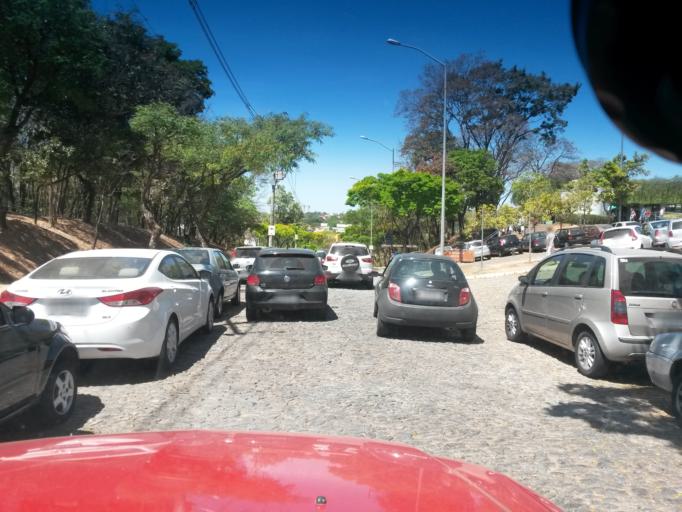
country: BR
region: Minas Gerais
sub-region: Belo Horizonte
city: Belo Horizonte
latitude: -19.8698
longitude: -43.9672
